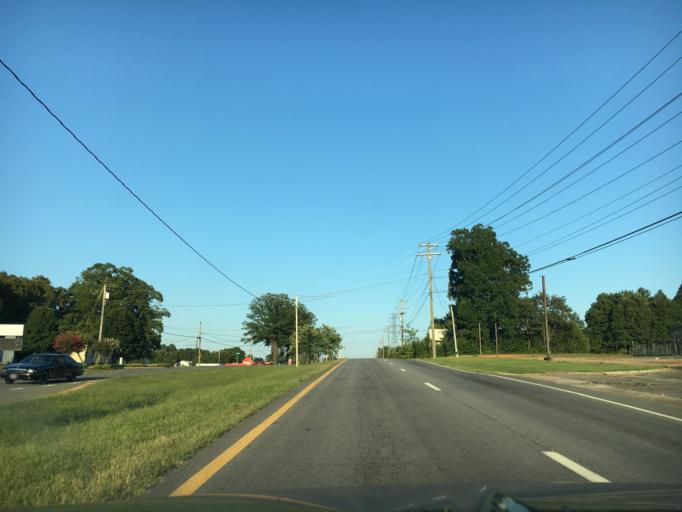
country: US
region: Virginia
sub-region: City of Danville
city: Danville
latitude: 36.5808
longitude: -79.3128
